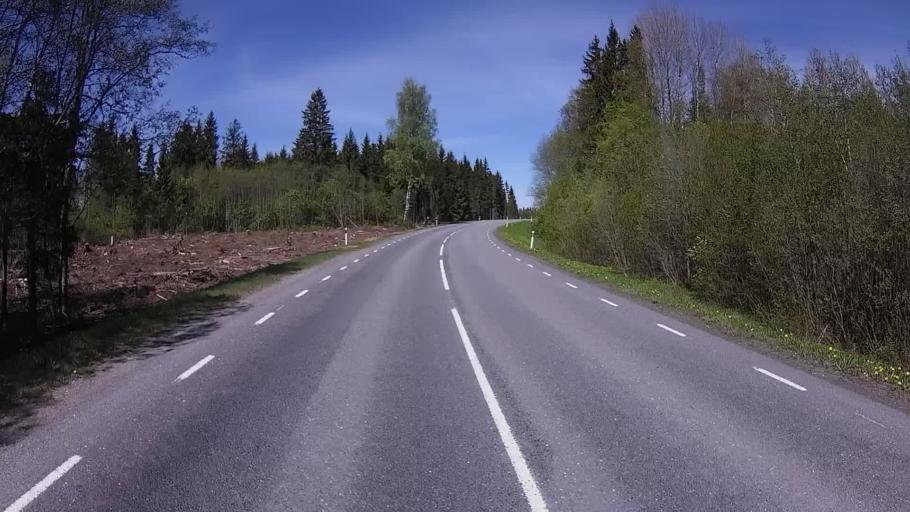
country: EE
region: Raplamaa
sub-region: Kehtna vald
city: Kehtna
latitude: 59.0466
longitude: 25.0241
